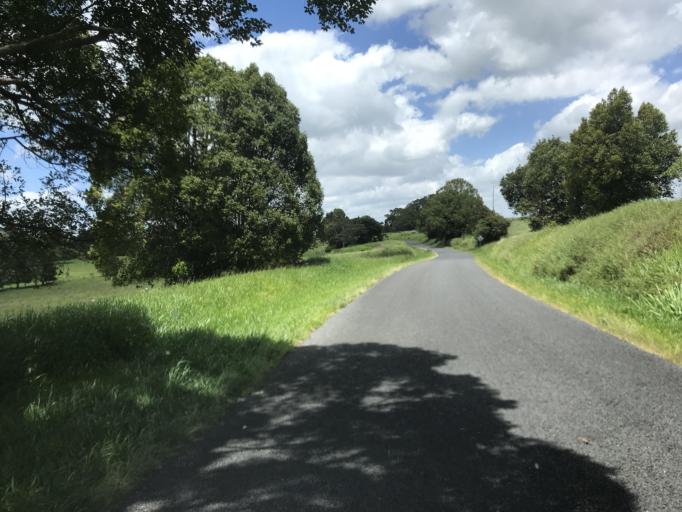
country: AU
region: Queensland
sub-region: Tablelands
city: Atherton
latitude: -17.3390
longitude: 145.5864
